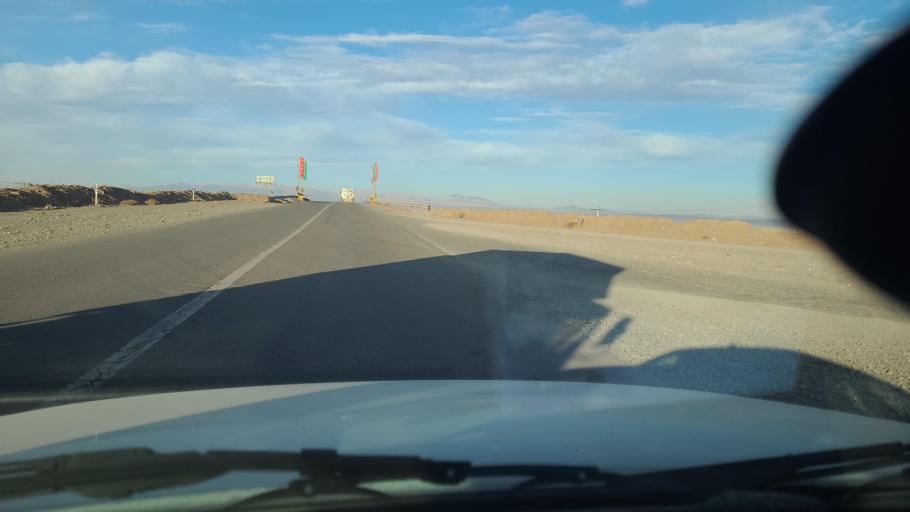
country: IR
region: Razavi Khorasan
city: Neqab
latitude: 36.6024
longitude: 57.5901
